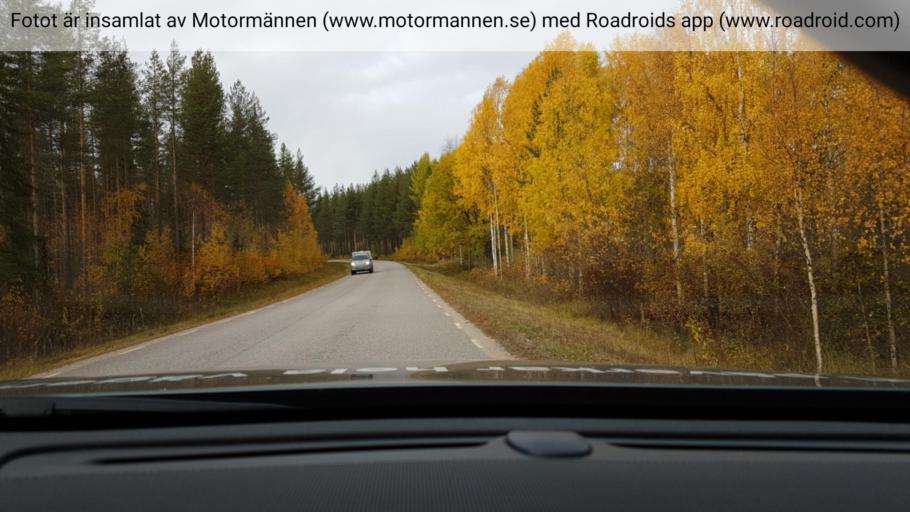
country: SE
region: Norrbotten
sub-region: Overkalix Kommun
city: OEverkalix
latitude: 66.2588
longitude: 23.1108
